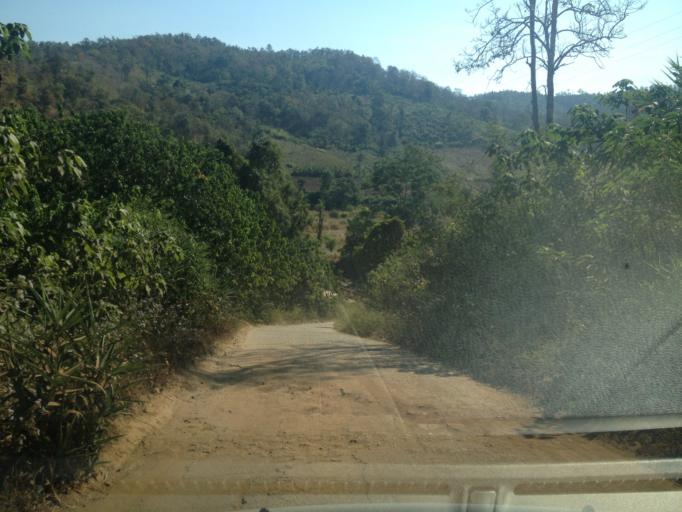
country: TH
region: Mae Hong Son
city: Ban Huai I Huak
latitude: 18.0633
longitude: 98.1817
